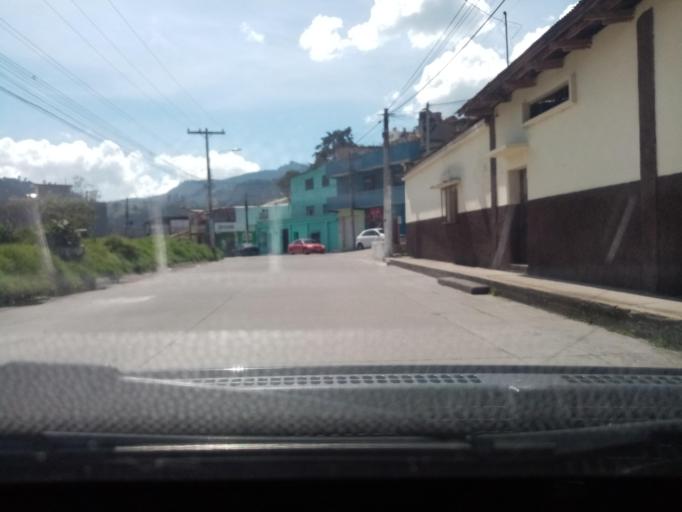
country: GT
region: Quetzaltenango
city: Quetzaltenango
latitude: 14.8405
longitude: -91.5124
